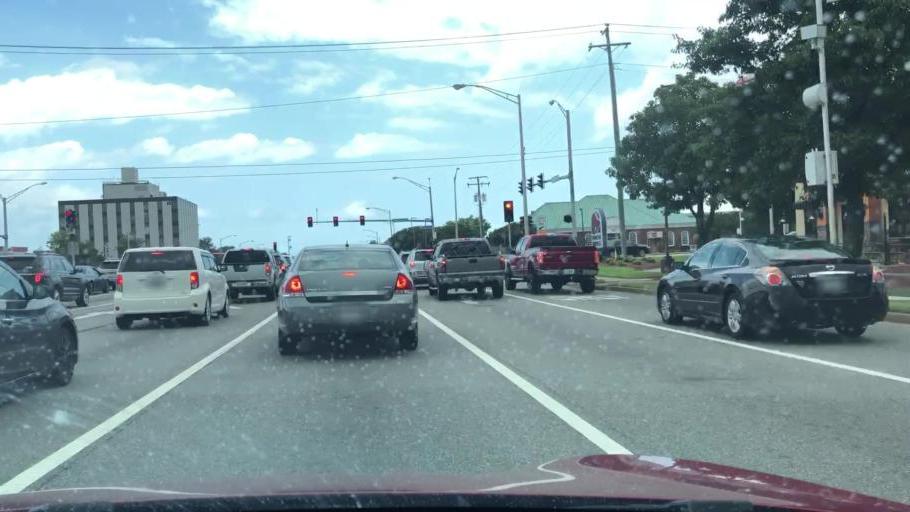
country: US
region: Virginia
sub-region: City of Chesapeake
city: Chesapeake
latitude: 36.8428
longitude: -76.1367
